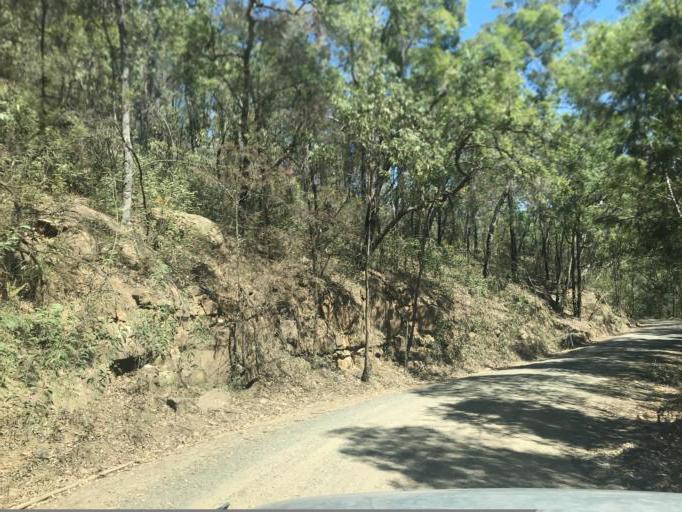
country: AU
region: New South Wales
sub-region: Wyong Shire
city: Little Jilliby
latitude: -33.1599
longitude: 151.0748
